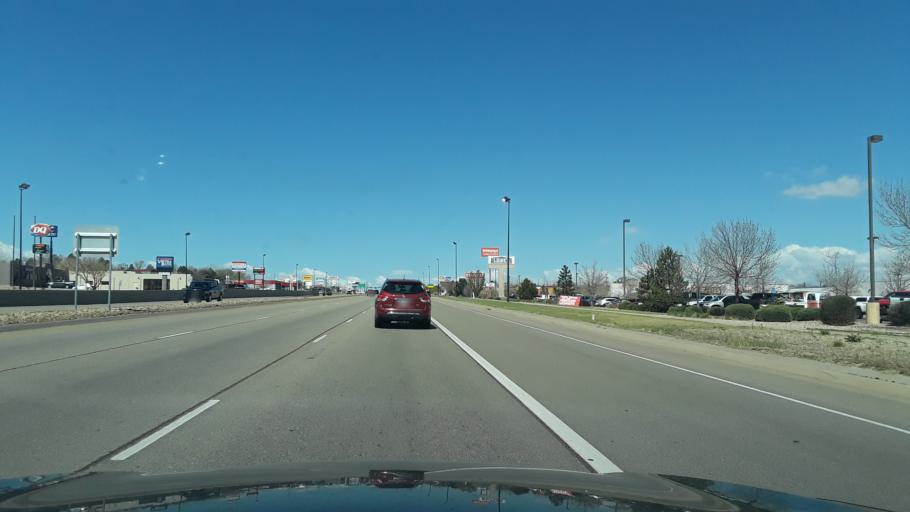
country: US
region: Colorado
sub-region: Pueblo County
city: Pueblo
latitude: 38.3085
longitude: -104.6225
